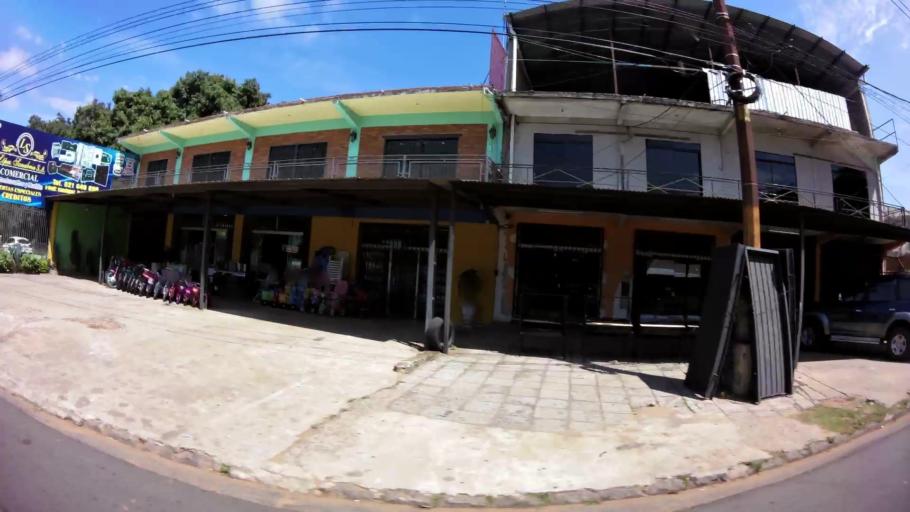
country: PY
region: Central
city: San Lorenzo
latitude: -25.3072
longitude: -57.5053
